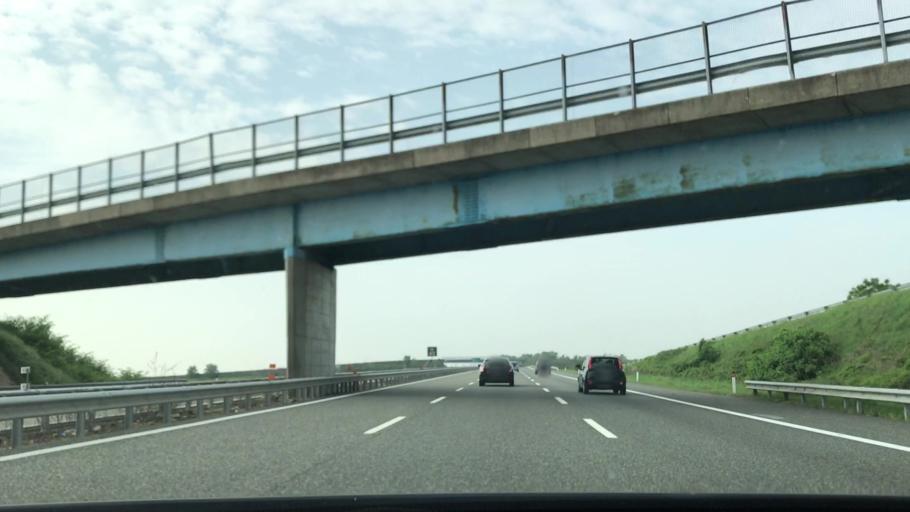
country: IT
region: Piedmont
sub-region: Provincia di Vercelli
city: Prarolo
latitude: 45.2698
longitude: 8.4691
